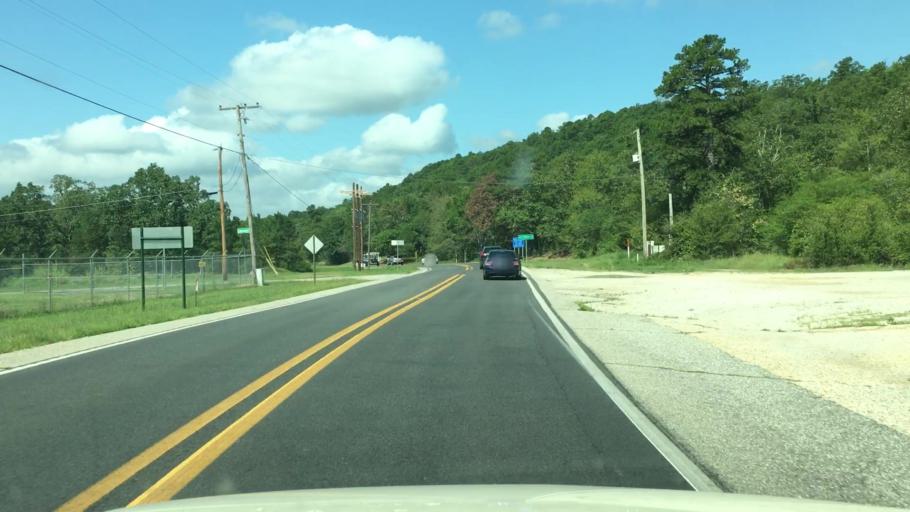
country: US
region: Arkansas
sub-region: Garland County
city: Lake Hamilton
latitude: 34.3915
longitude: -93.1155
